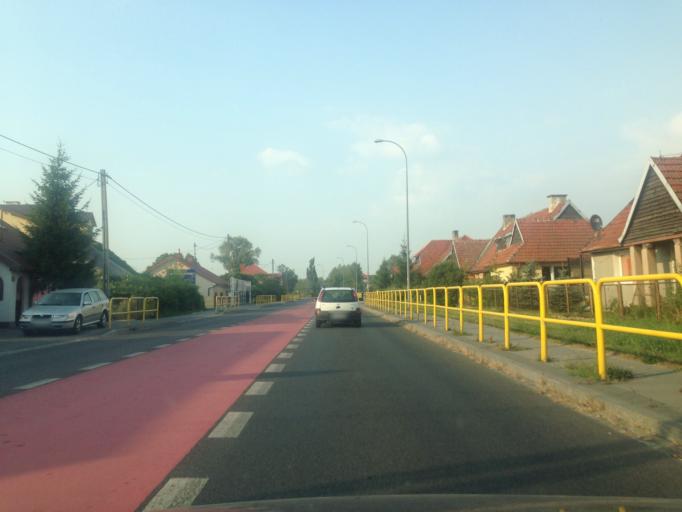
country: PL
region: Kujawsko-Pomorskie
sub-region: Powiat wloclawski
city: Fabianki
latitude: 52.7172
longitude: 19.1081
